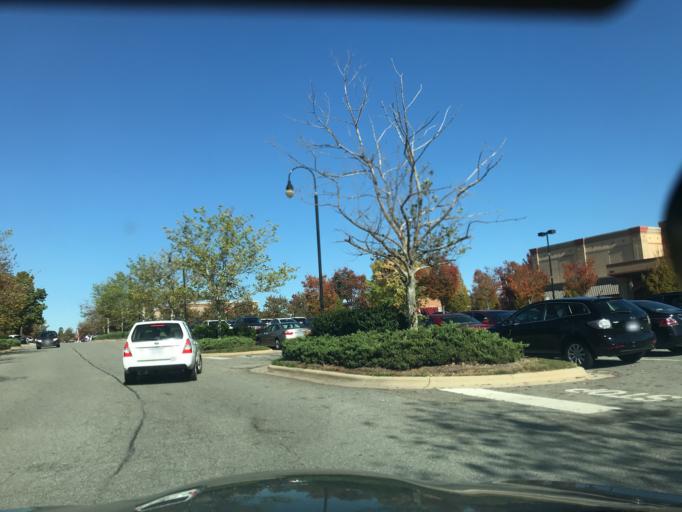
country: US
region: North Carolina
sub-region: Wake County
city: Morrisville
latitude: 35.9040
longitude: -78.7854
